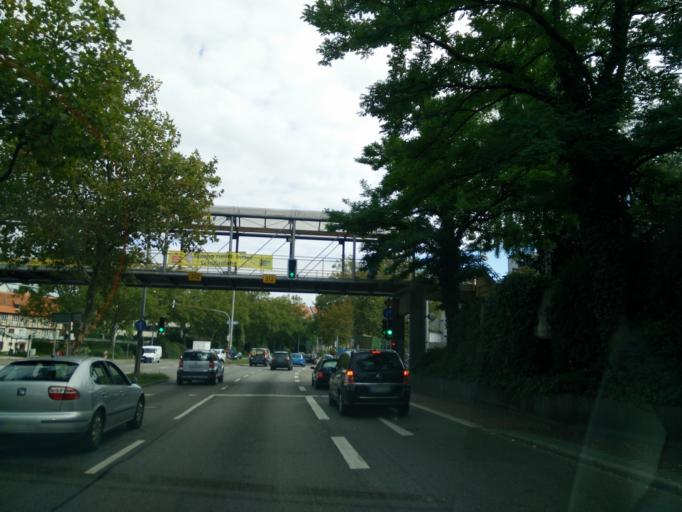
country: DE
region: Baden-Wuerttemberg
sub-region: Tuebingen Region
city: Reutlingen
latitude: 48.4906
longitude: 9.2074
